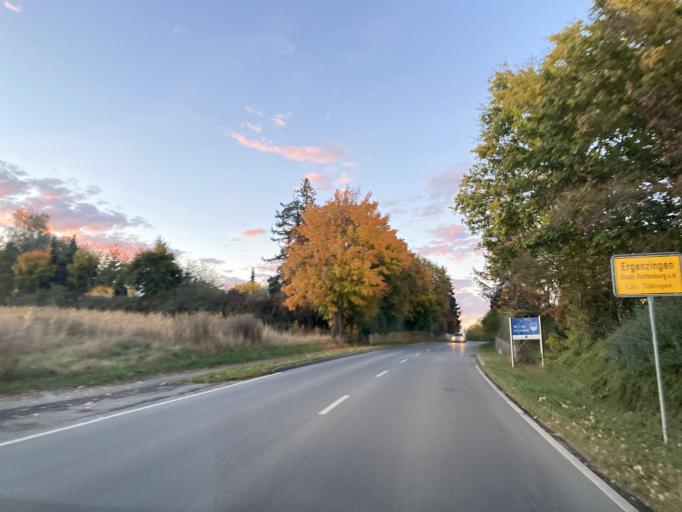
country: DE
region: Baden-Wuerttemberg
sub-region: Regierungsbezirk Stuttgart
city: Bondorf
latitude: 48.4892
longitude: 8.8124
